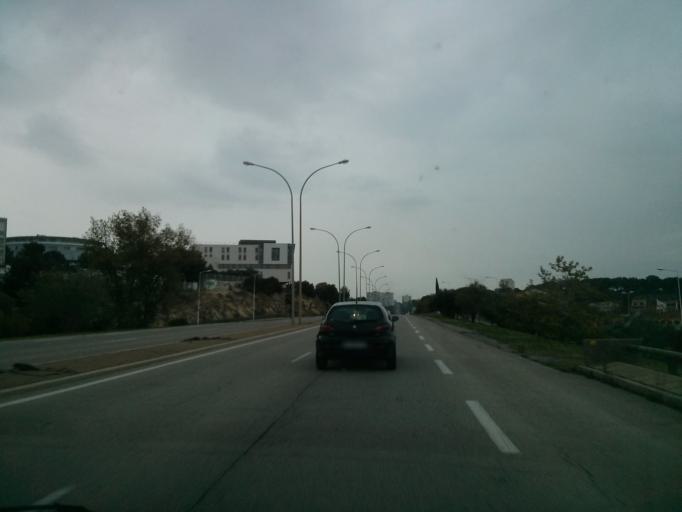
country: FR
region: Languedoc-Roussillon
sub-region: Departement du Gard
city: Milhaud
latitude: 43.8198
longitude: 4.3207
